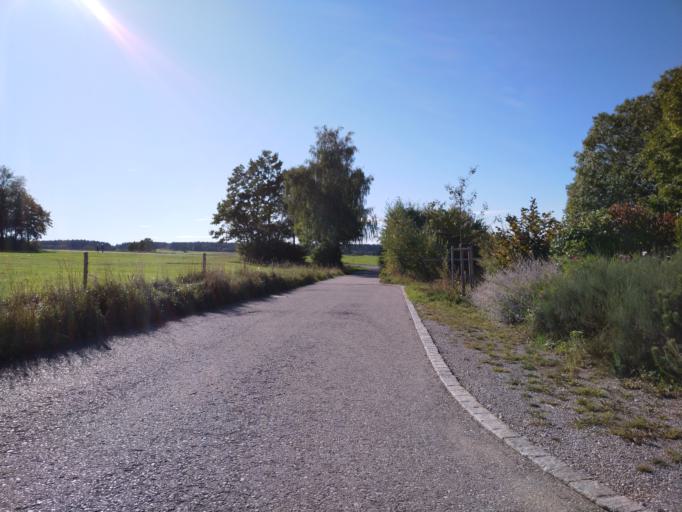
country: DE
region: Bavaria
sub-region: Swabia
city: Irsee
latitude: 47.9023
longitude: 10.5700
